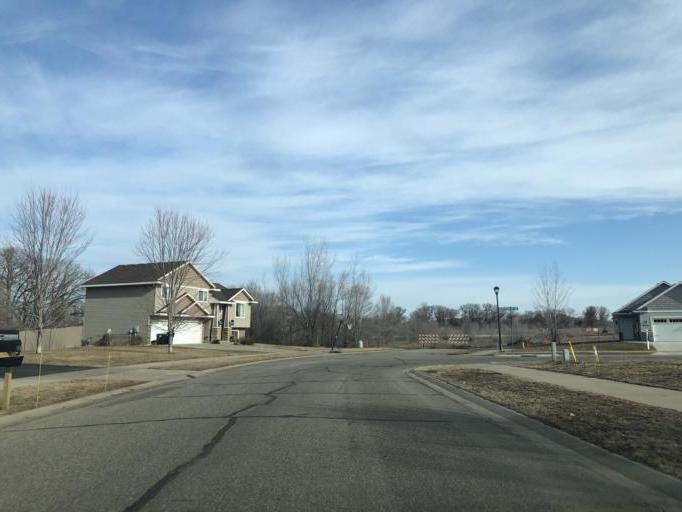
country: US
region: Minnesota
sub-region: Sherburne County
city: Becker
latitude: 45.4012
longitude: -93.8538
